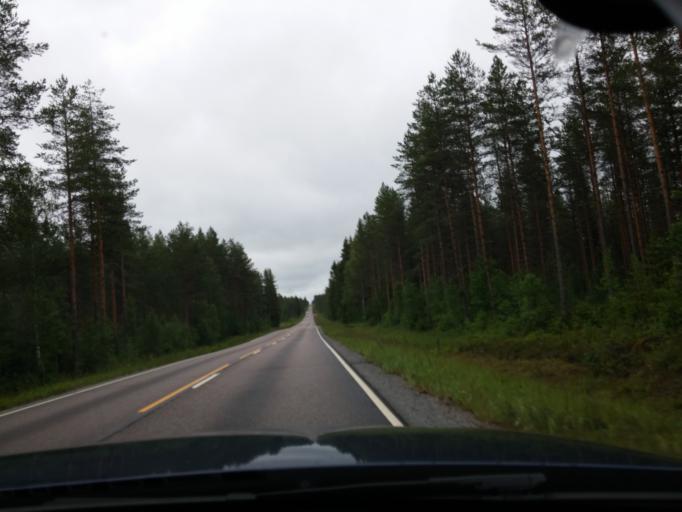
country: FI
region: Central Finland
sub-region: Saarijaervi-Viitasaari
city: Pylkoenmaeki
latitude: 62.5935
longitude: 24.6032
